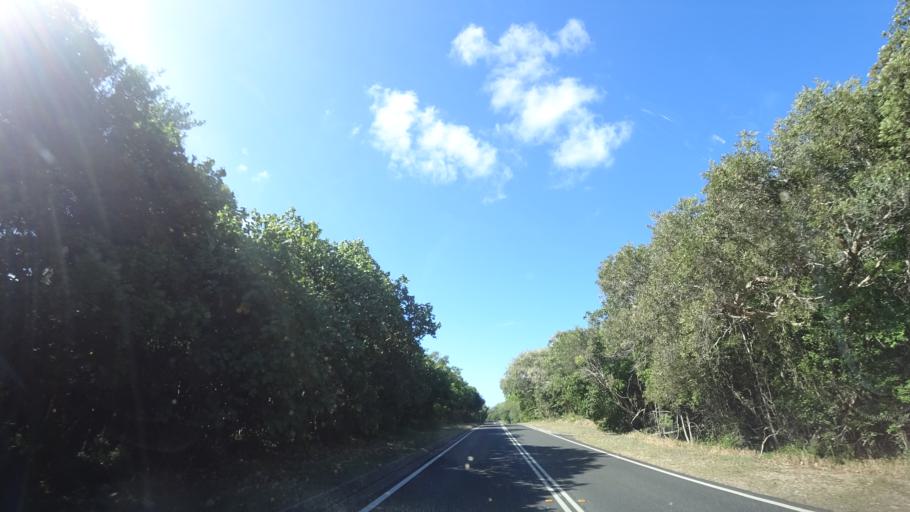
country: AU
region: Queensland
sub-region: Sunshine Coast
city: Mooloolaba
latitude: -26.6345
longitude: 153.1004
